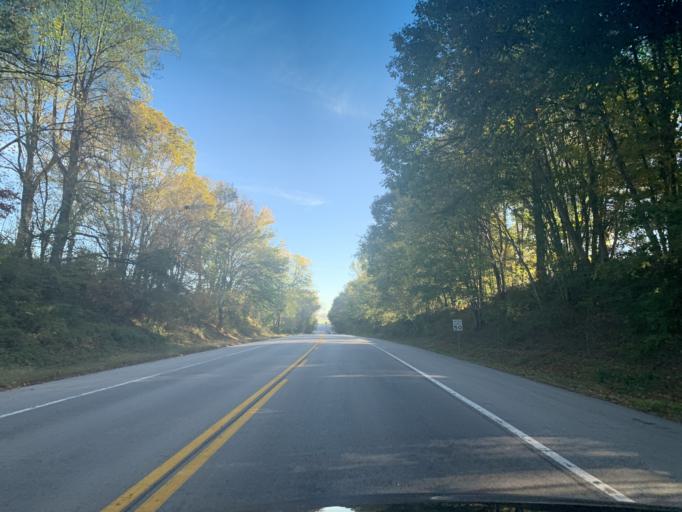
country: US
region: Maryland
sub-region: Cecil County
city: Rising Sun
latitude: 39.6971
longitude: -76.0898
